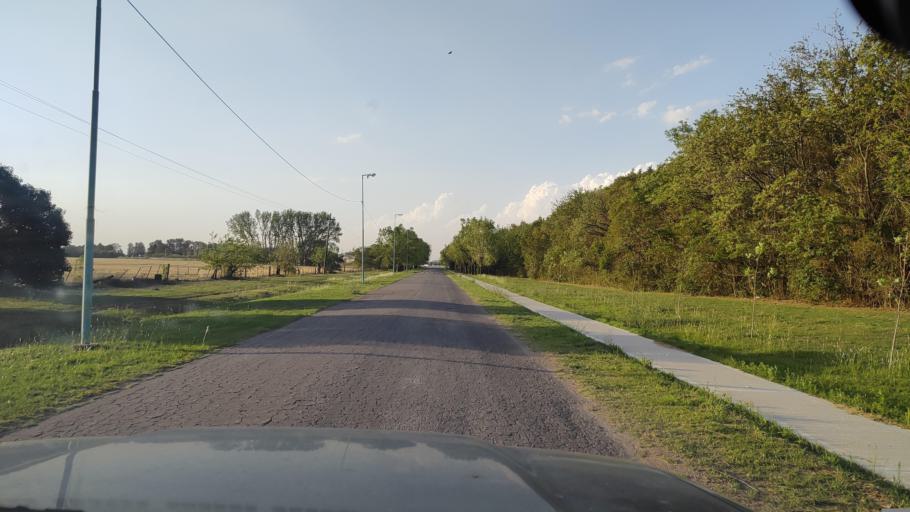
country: AR
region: Buenos Aires
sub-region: Partido de Lujan
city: Lujan
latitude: -34.5492
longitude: -59.2097
